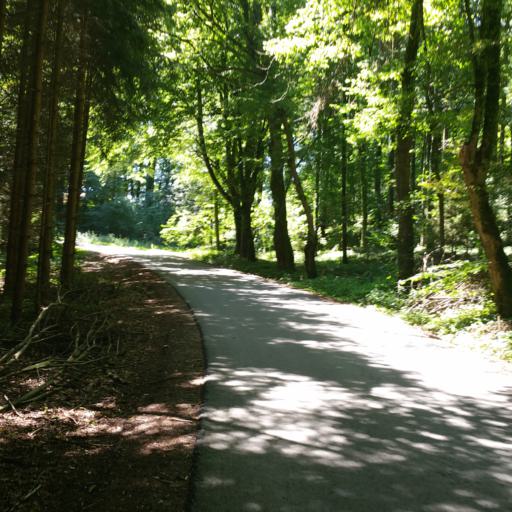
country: AT
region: Styria
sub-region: Politischer Bezirk Leibnitz
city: Gleinstatten
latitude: 46.7362
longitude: 15.3494
